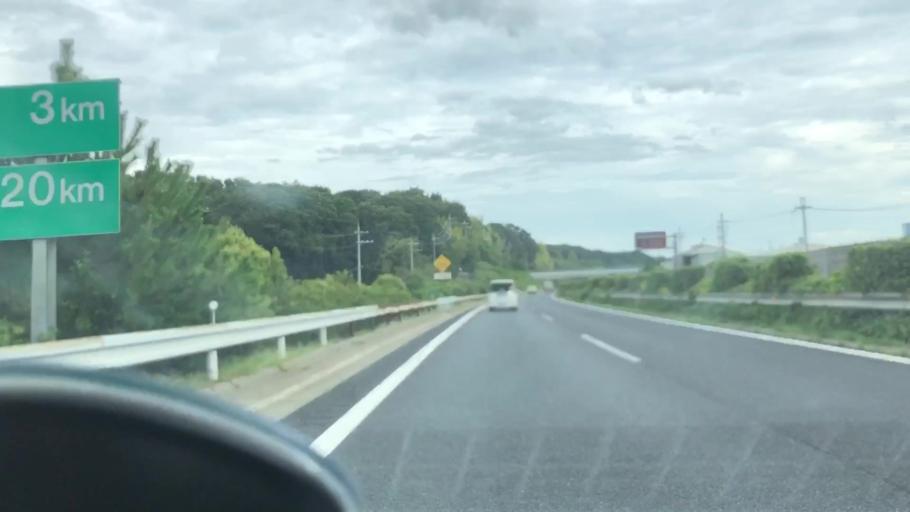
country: JP
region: Hyogo
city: Yashiro
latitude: 34.9316
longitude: 134.9692
